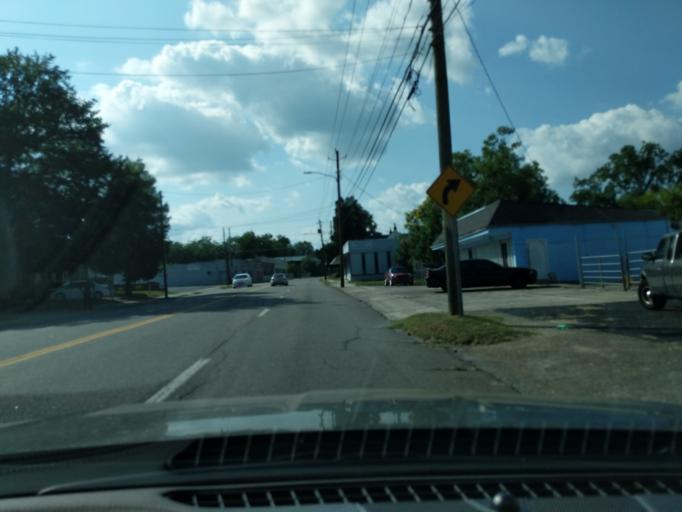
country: US
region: Georgia
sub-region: Richmond County
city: Augusta
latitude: 33.4872
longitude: -82.0015
